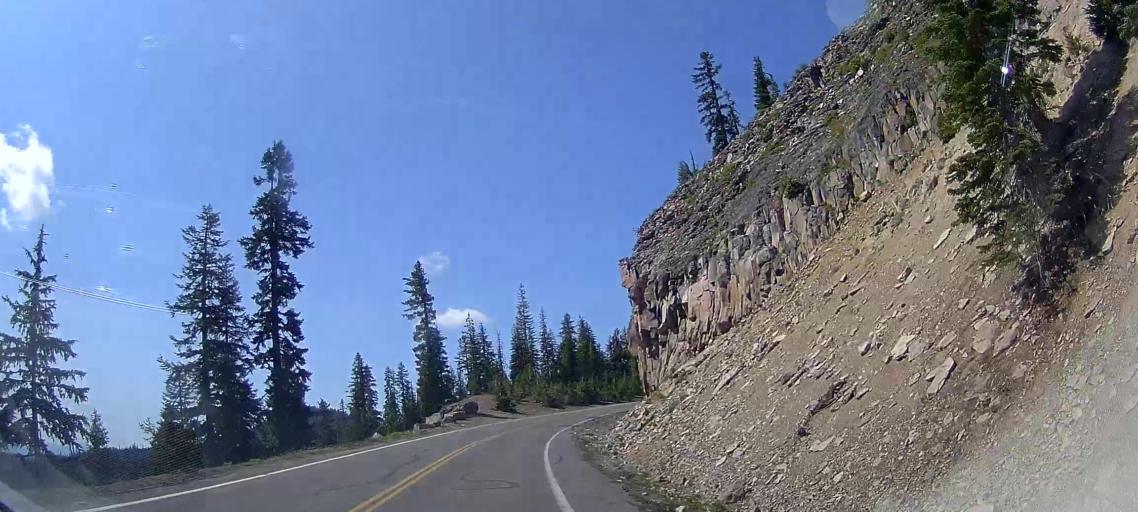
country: US
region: Oregon
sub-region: Klamath County
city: Klamath Falls
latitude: 42.8772
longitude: -122.1041
